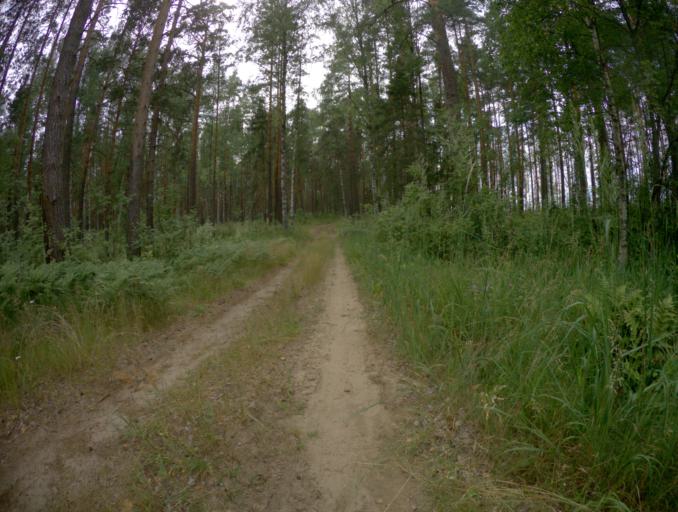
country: RU
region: Vladimir
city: Gorokhovets
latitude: 56.3011
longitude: 42.6878
